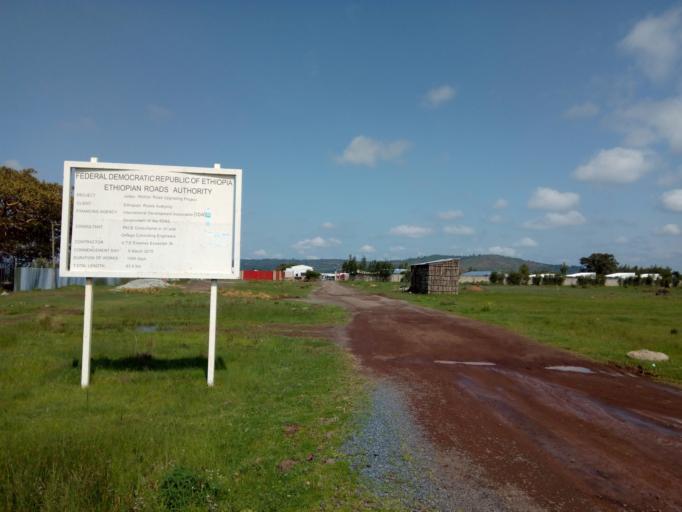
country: ET
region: Oromiya
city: Waliso
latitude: 8.5572
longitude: 37.9494
